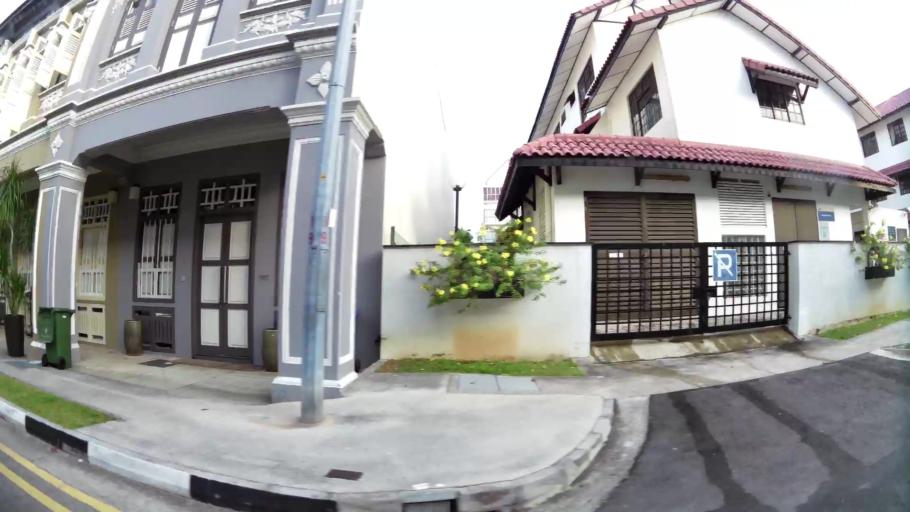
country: SG
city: Singapore
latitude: 1.3141
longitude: 103.9049
